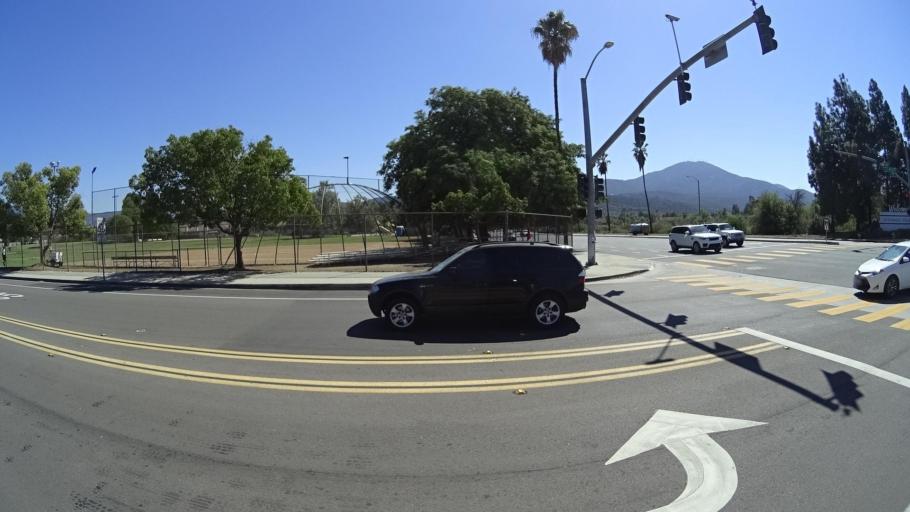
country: US
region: California
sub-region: San Diego County
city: Rancho San Diego
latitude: 32.7474
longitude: -116.9369
